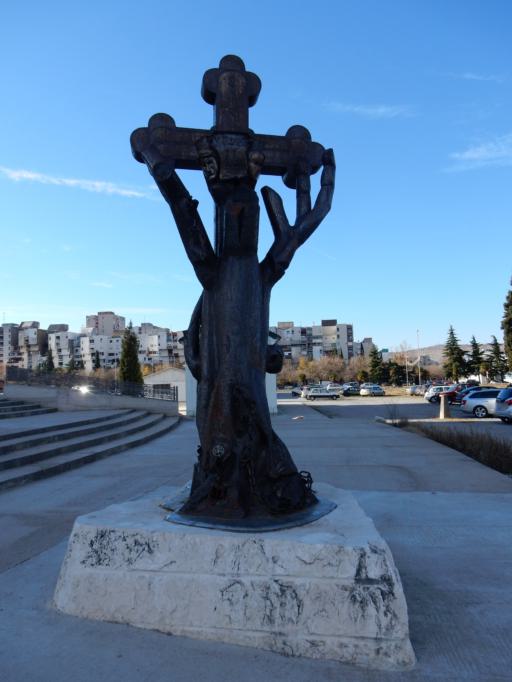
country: ME
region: Podgorica
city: Podgorica
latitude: 42.4460
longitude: 19.2486
